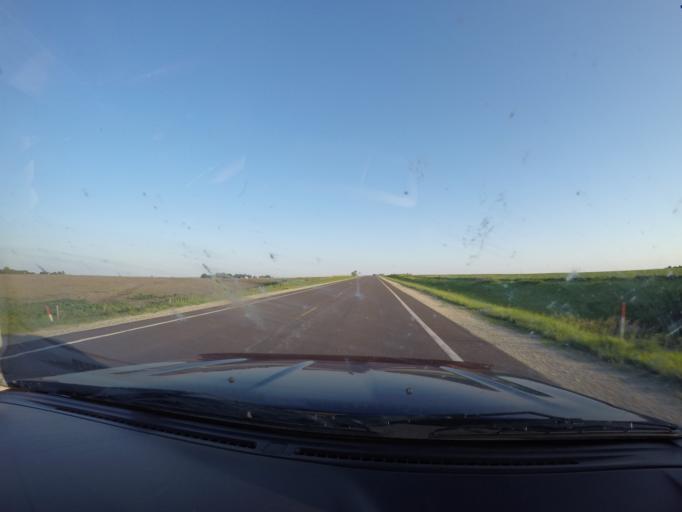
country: US
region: Kansas
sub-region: Marshall County
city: Blue Rapids
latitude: 39.6450
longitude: -96.7506
